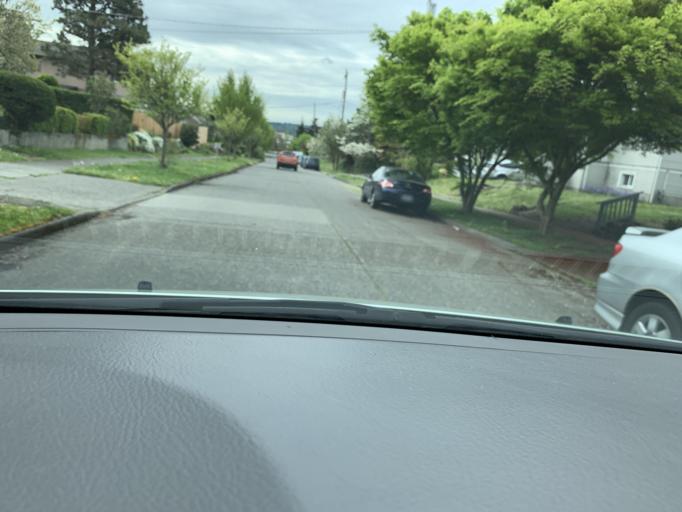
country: US
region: Washington
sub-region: King County
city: White Center
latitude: 47.5510
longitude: -122.3123
